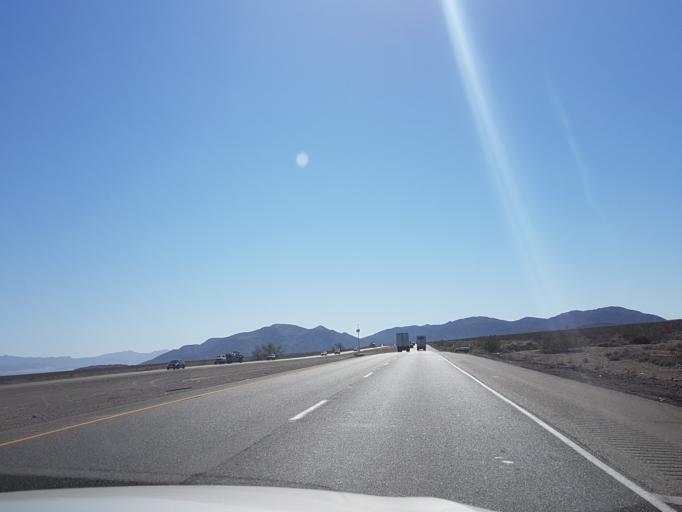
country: US
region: California
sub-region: San Bernardino County
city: Fort Irwin
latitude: 35.2352
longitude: -116.1005
